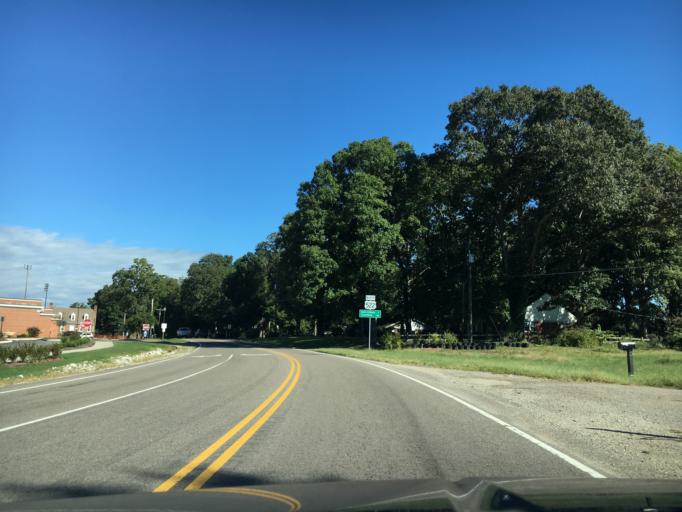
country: US
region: Virginia
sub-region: Goochland County
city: Goochland
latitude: 37.6936
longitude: -77.8873
